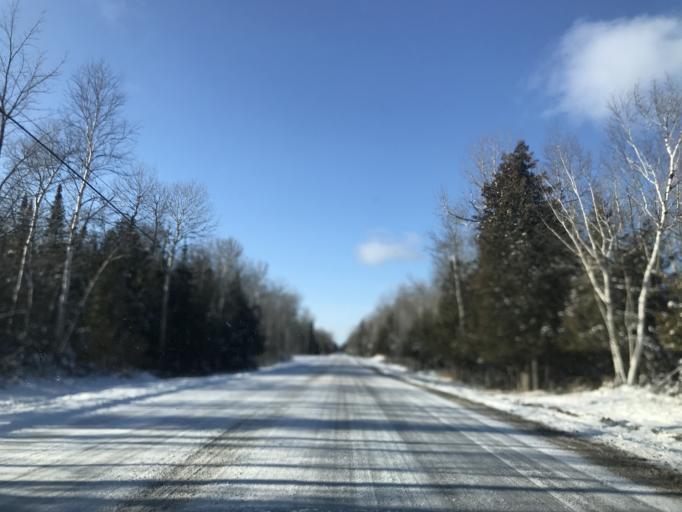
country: US
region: Wisconsin
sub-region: Door County
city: Sturgeon Bay
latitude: 44.8496
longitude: -87.4849
